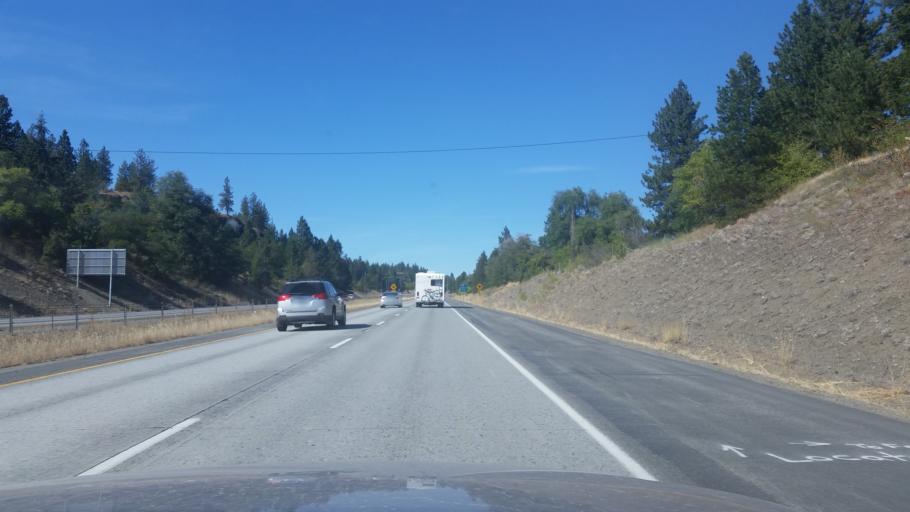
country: US
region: Washington
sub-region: Spokane County
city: Spokane
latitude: 47.6285
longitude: -117.4421
